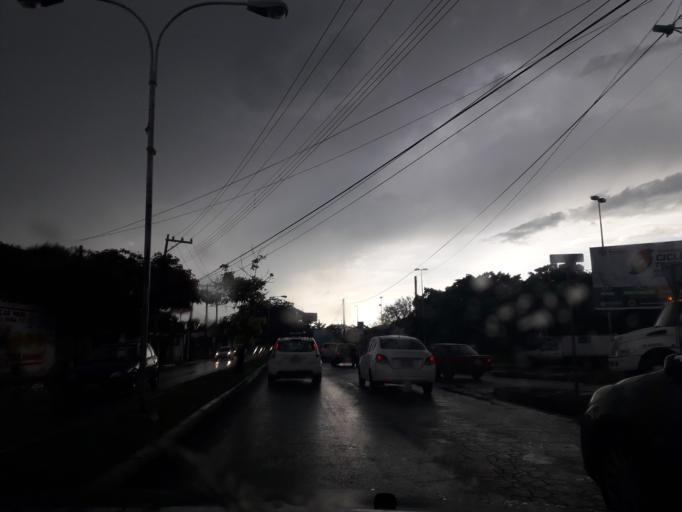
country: MX
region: Yucatan
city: Merida
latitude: 20.9772
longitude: -89.6436
